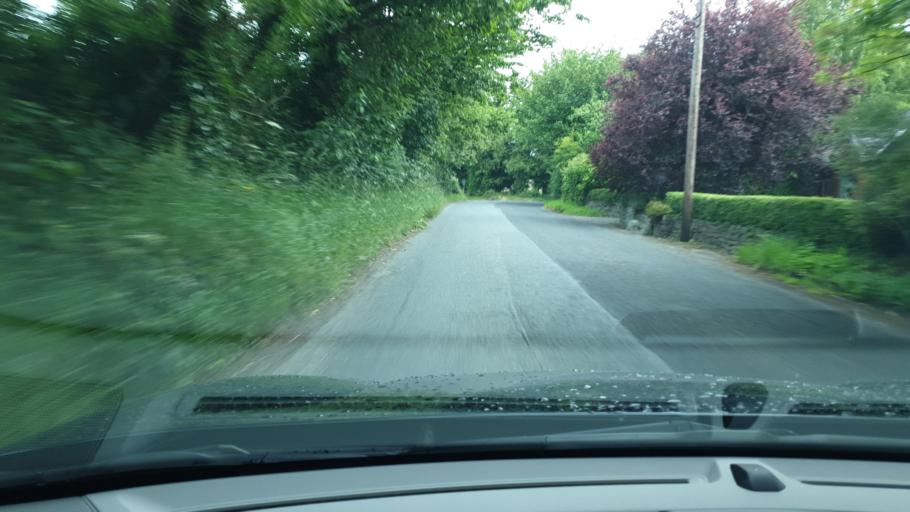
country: IE
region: Leinster
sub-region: An Mhi
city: Ashbourne
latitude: 53.5350
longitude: -6.3896
